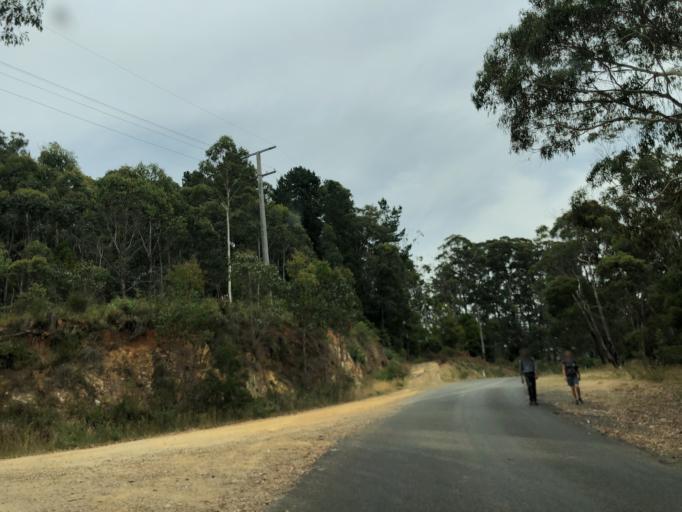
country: AU
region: Victoria
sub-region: Moorabool
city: Bacchus Marsh
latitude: -37.4726
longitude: 144.2979
